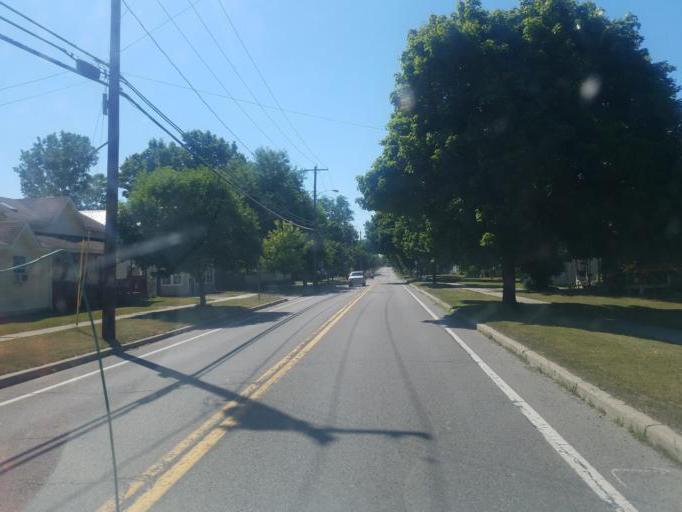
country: US
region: New York
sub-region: Ontario County
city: Phelps
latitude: 42.9602
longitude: -77.0663
